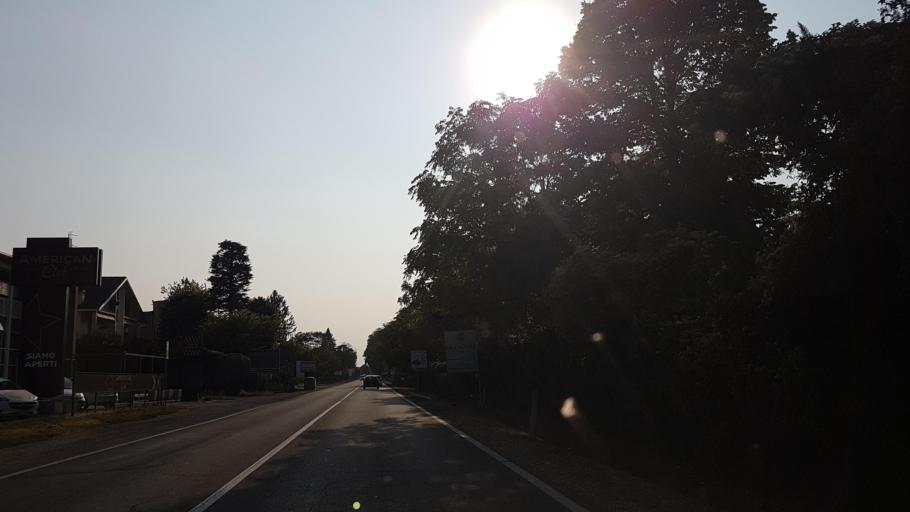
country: IT
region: Emilia-Romagna
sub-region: Provincia di Parma
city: Vicofertile
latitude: 44.7767
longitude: 10.2767
